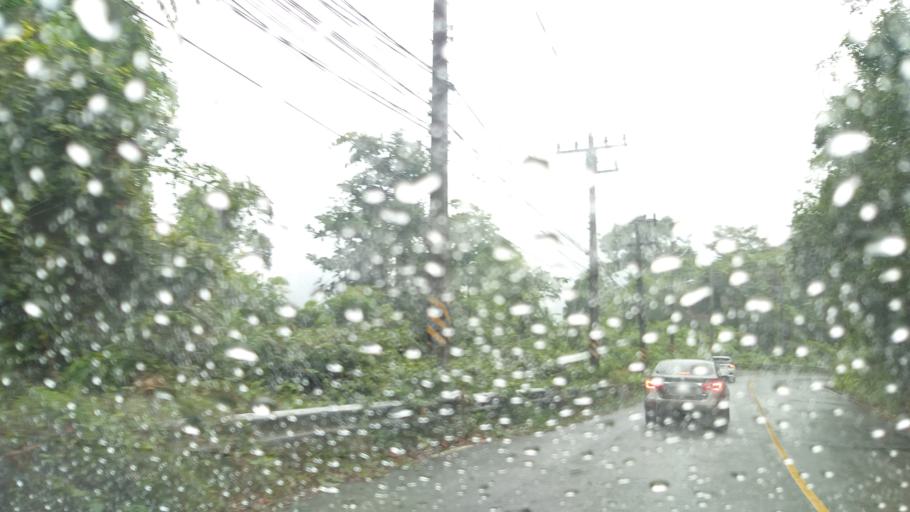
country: TH
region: Trat
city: Laem Ngop
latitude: 12.1235
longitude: 102.2669
